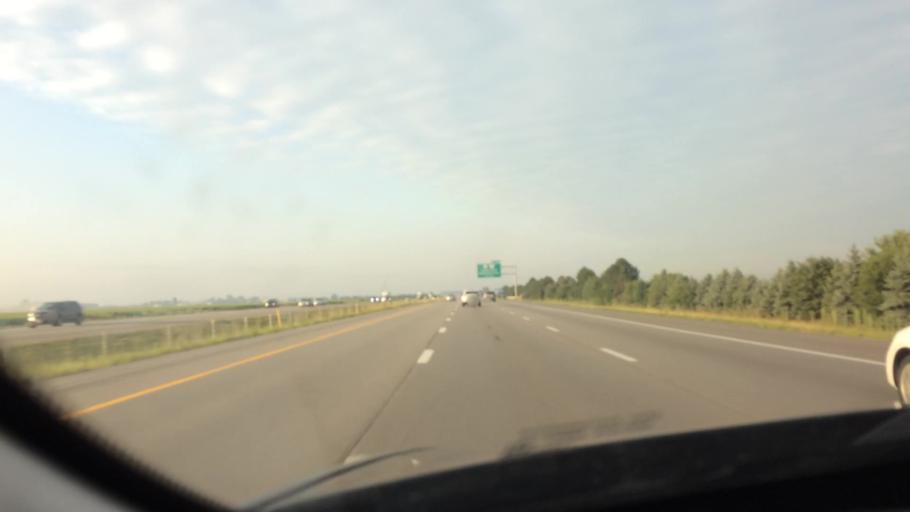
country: US
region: Ohio
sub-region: Wood County
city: Bowling Green
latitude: 41.3991
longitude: -83.6161
